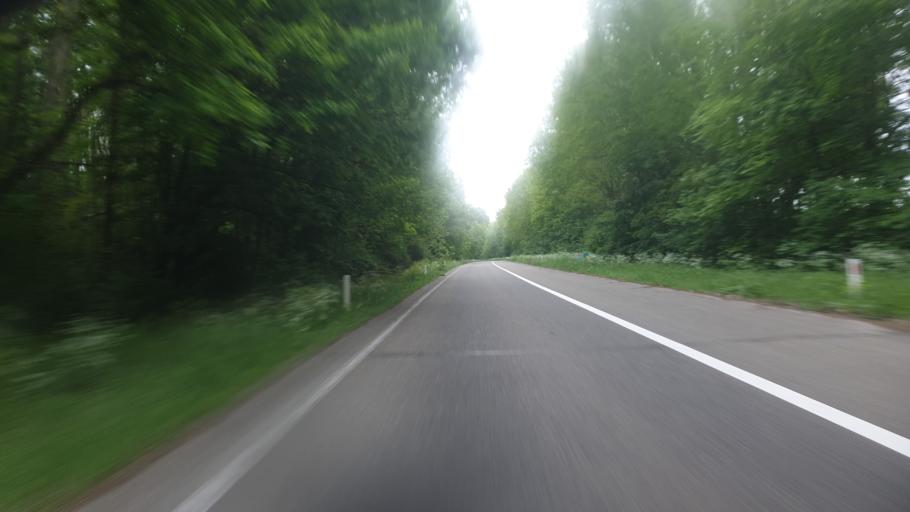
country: NL
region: Gelderland
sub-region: Gemeente Overbetuwe
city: Elst
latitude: 51.8941
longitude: 5.8669
